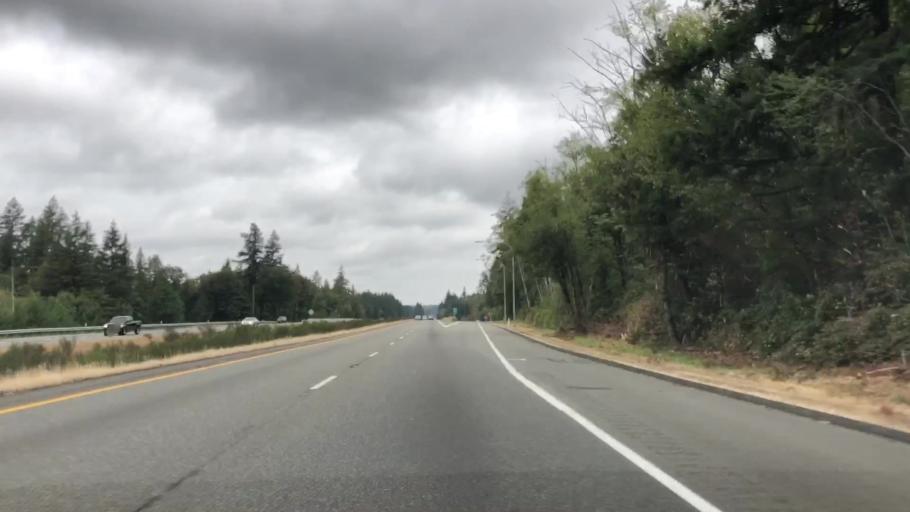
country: US
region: Washington
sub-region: Kitsap County
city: Burley
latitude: 47.4283
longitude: -122.6232
